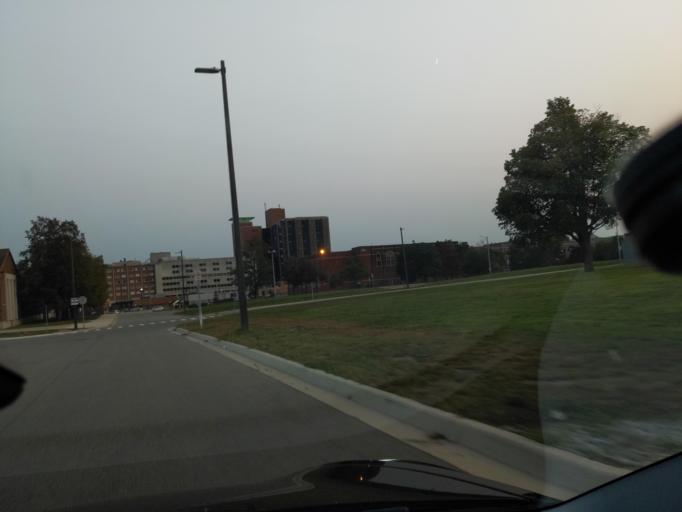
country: US
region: Michigan
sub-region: Ingham County
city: Lansing
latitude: 42.7375
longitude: -84.5347
